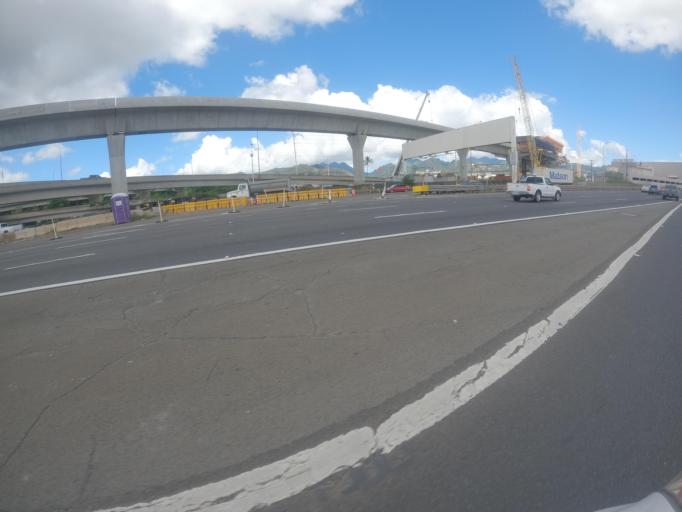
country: US
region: Hawaii
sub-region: Honolulu County
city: Honolulu
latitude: 21.3326
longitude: -157.8905
